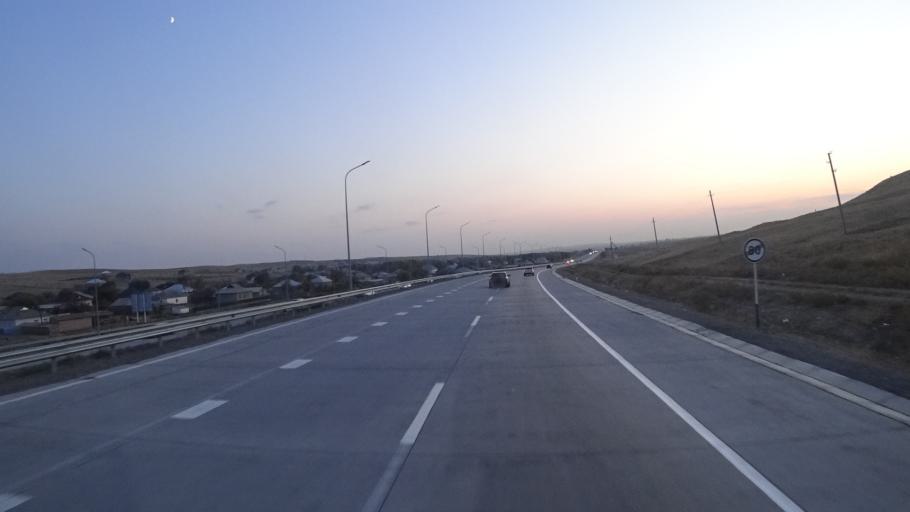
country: KZ
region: Ongtustik Qazaqstan
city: Qazyqurt
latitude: 41.8964
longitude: 69.4531
